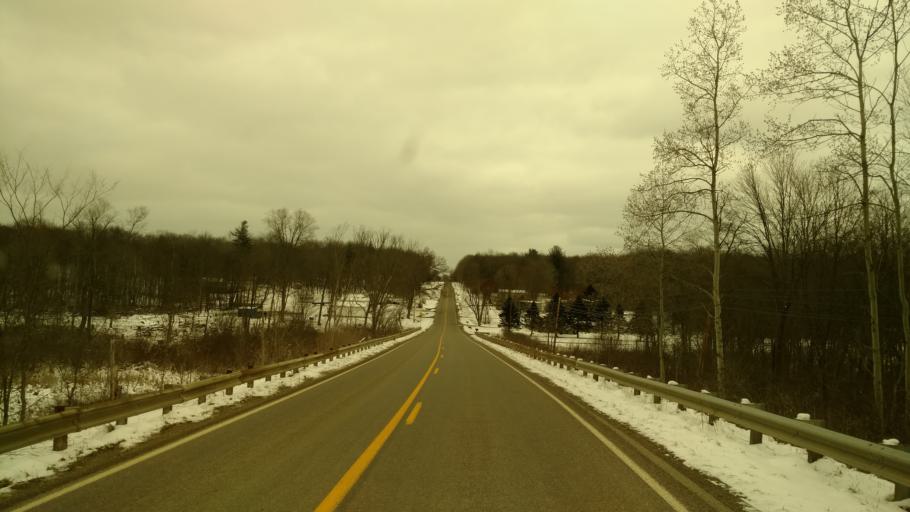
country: US
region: Pennsylvania
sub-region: Mercer County
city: Mercer
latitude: 41.3242
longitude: -80.2435
